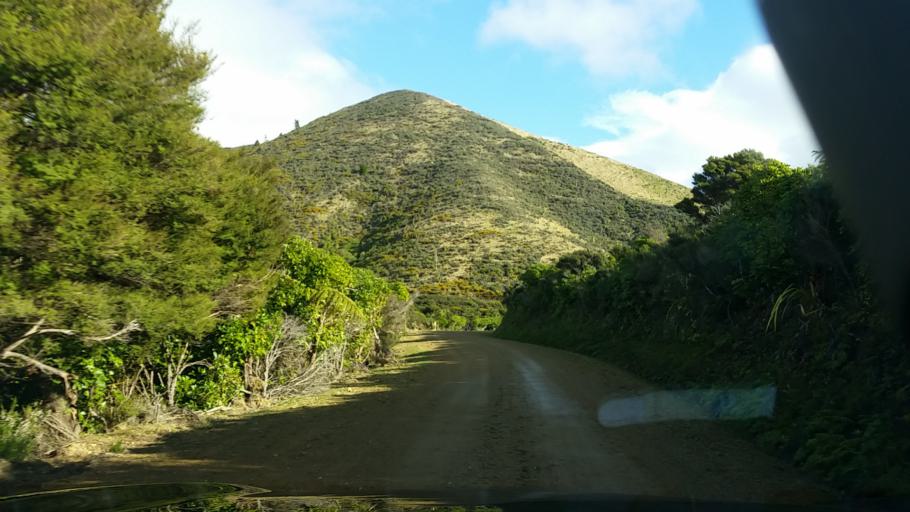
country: NZ
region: Marlborough
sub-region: Marlborough District
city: Picton
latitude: -40.9671
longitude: 173.8957
